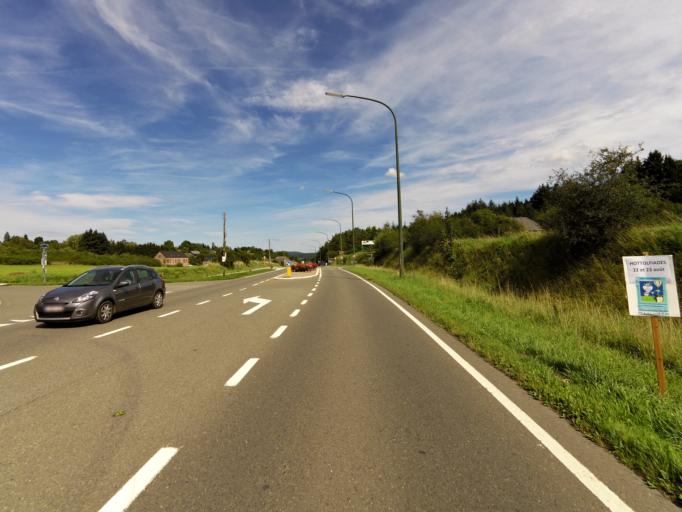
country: BE
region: Wallonia
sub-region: Province du Luxembourg
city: Hotton
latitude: 50.2614
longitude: 5.4339
